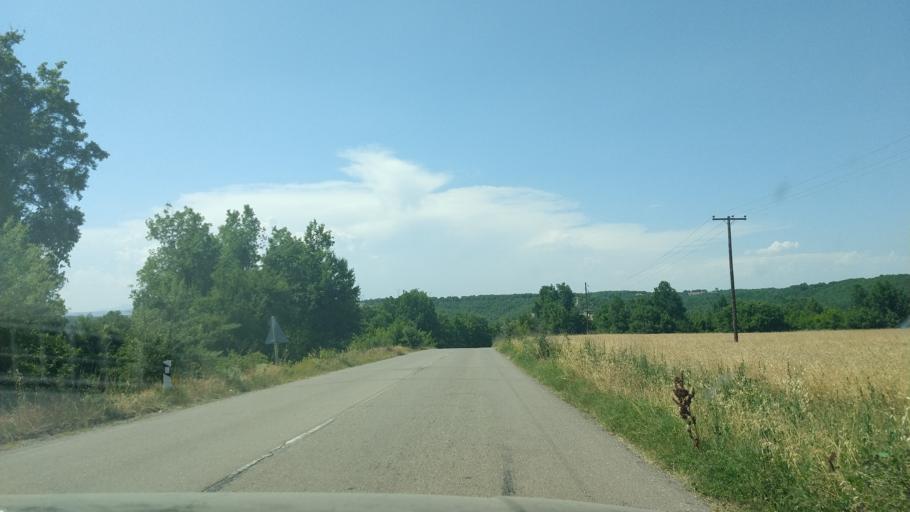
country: GR
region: West Macedonia
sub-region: Nomos Grevenon
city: Grevena
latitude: 40.0435
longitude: 21.4831
